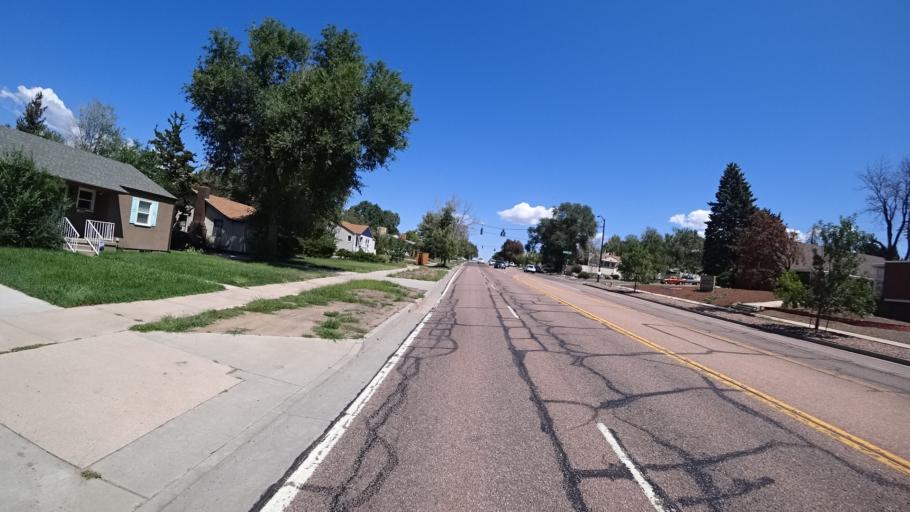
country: US
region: Colorado
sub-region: El Paso County
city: Colorado Springs
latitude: 38.8484
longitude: -104.7943
